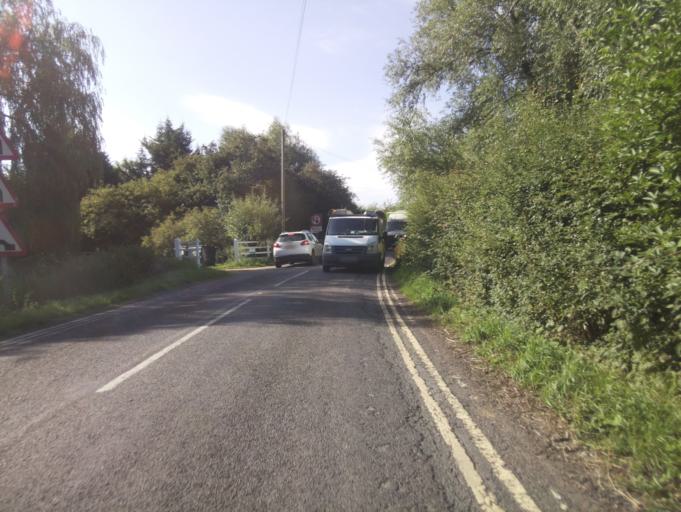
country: GB
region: England
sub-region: Oxfordshire
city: Faringdon
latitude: 51.6949
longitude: -1.5876
